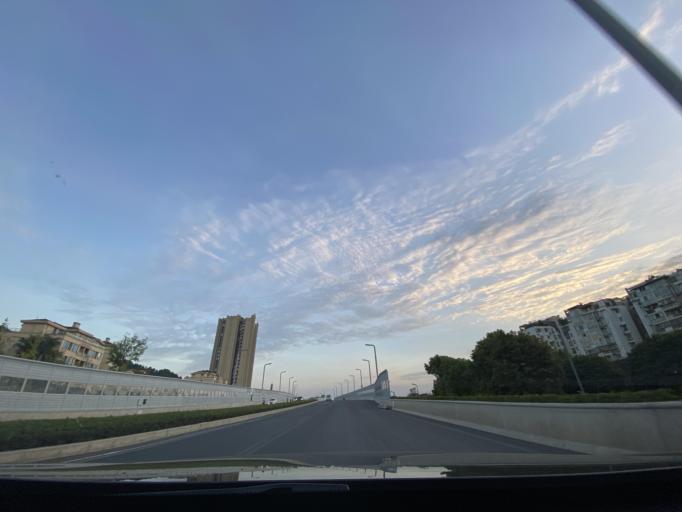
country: CN
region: Sichuan
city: Longquan
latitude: 30.6001
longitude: 104.3087
